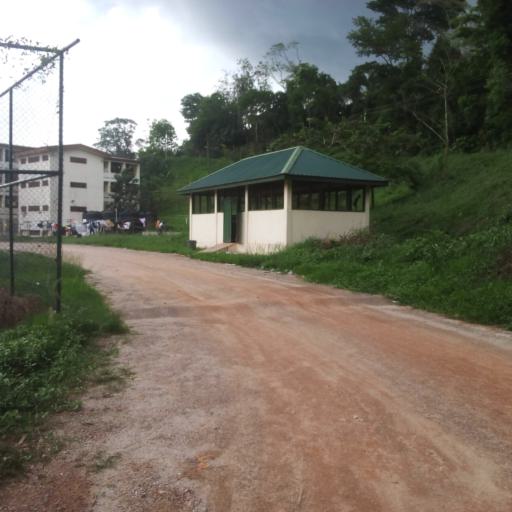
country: GH
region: Western
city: Tarkwa
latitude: 5.3004
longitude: -2.0030
